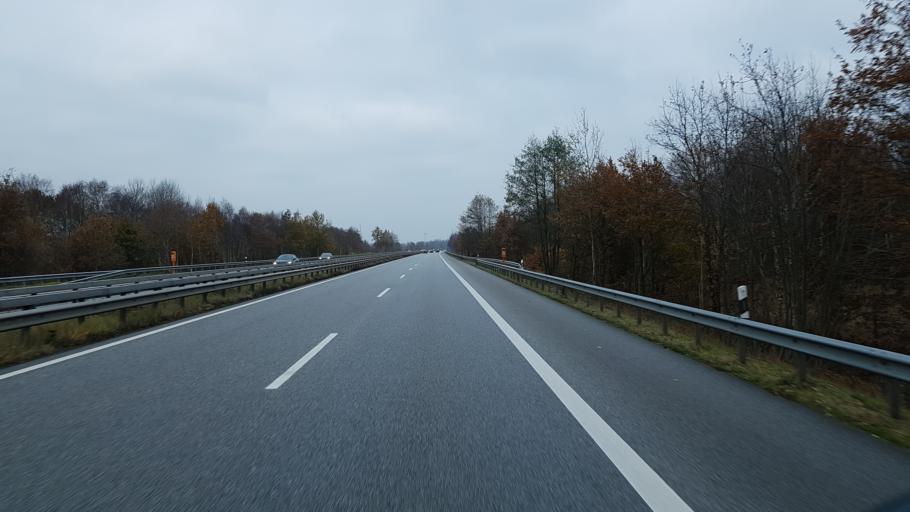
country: DE
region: Lower Saxony
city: Driftsethe
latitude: 53.4220
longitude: 8.5808
